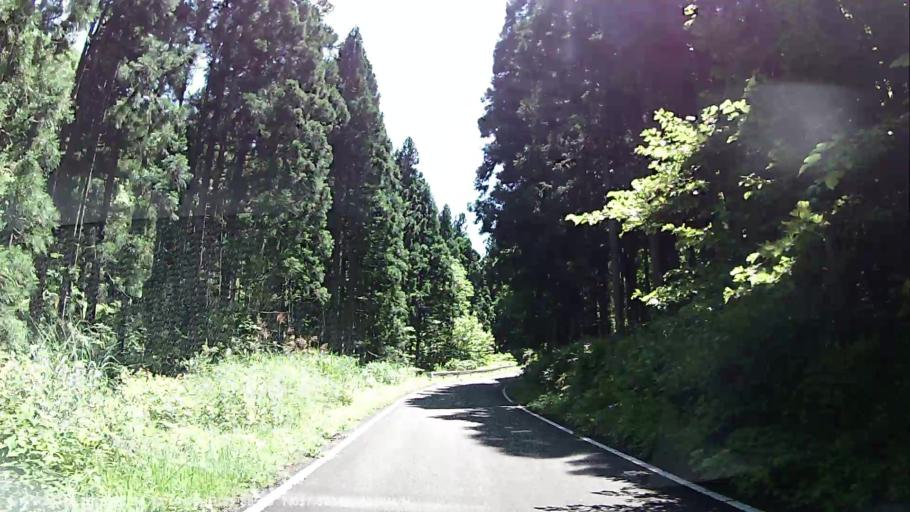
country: JP
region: Fukushima
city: Kitakata
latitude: 37.3834
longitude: 139.8551
